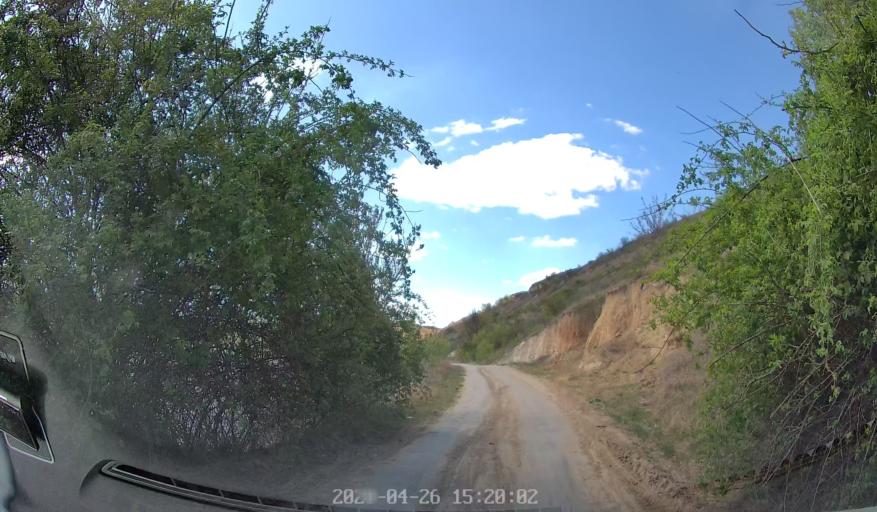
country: MD
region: Telenesti
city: Cocieri
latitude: 47.3635
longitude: 29.0974
